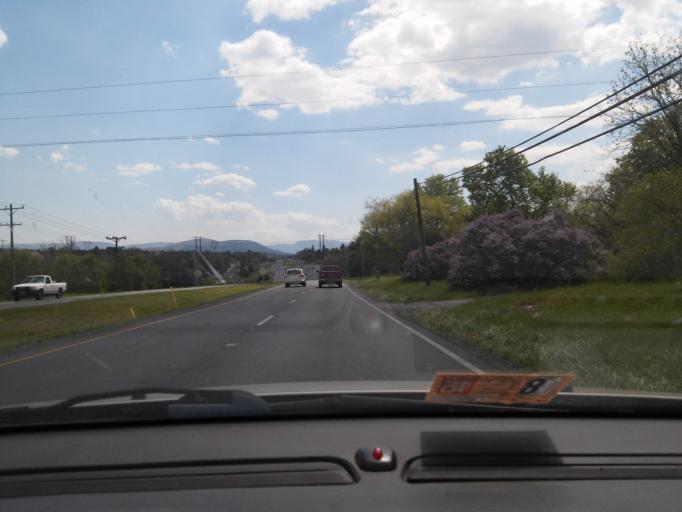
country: US
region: Virginia
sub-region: Warren County
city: Front Royal
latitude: 38.9821
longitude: -78.1831
